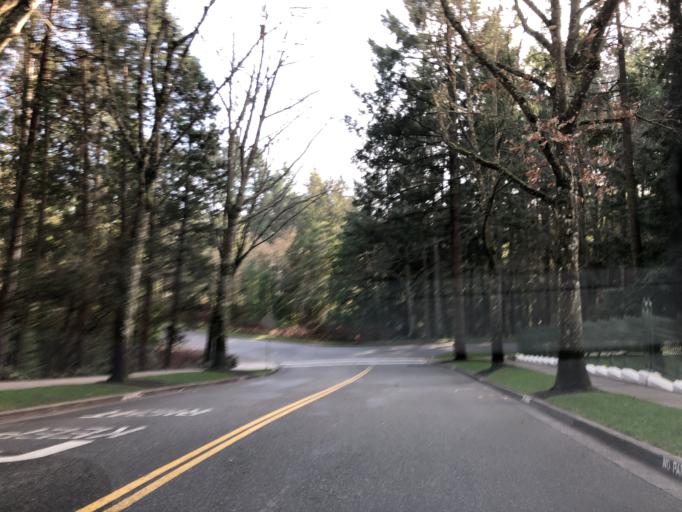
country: US
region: Oregon
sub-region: Washington County
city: Durham
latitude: 45.4255
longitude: -122.7411
